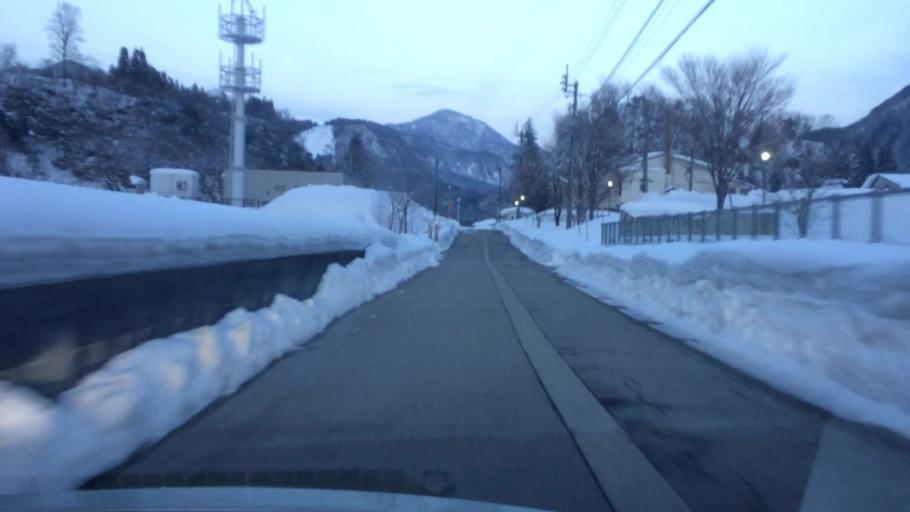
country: JP
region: Toyama
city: Kamiichi
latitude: 36.5741
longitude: 137.3824
